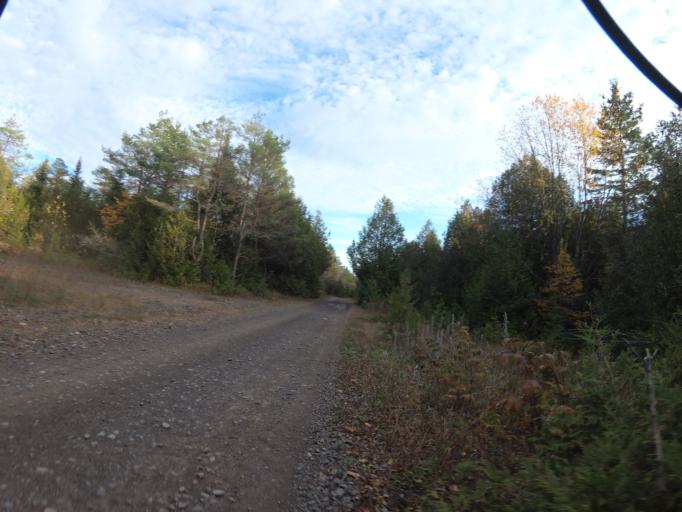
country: CA
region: Ontario
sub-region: Lanark County
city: Smiths Falls
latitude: 45.0184
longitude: -75.8081
